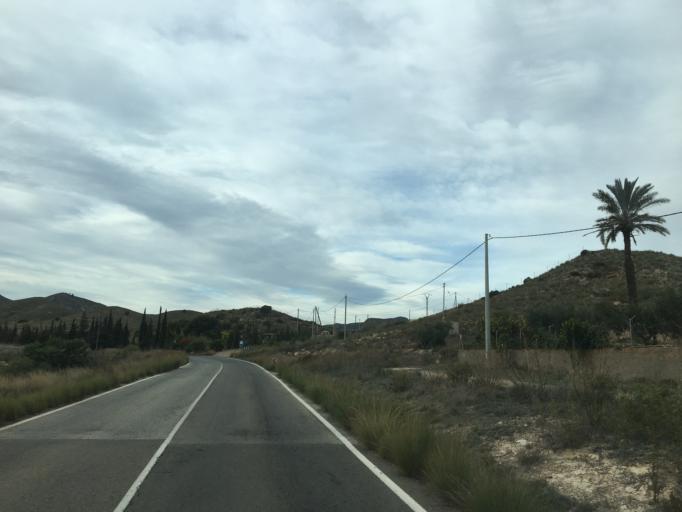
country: ES
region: Murcia
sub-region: Murcia
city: Fuente-Alamo de Murcia
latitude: 37.6150
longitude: -1.0964
